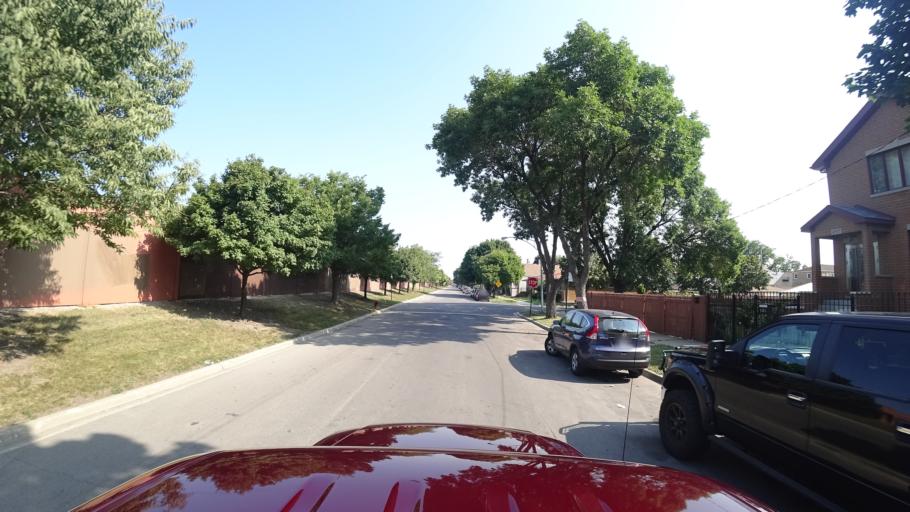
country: US
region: Illinois
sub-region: Cook County
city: Cicero
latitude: 41.8113
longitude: -87.7125
